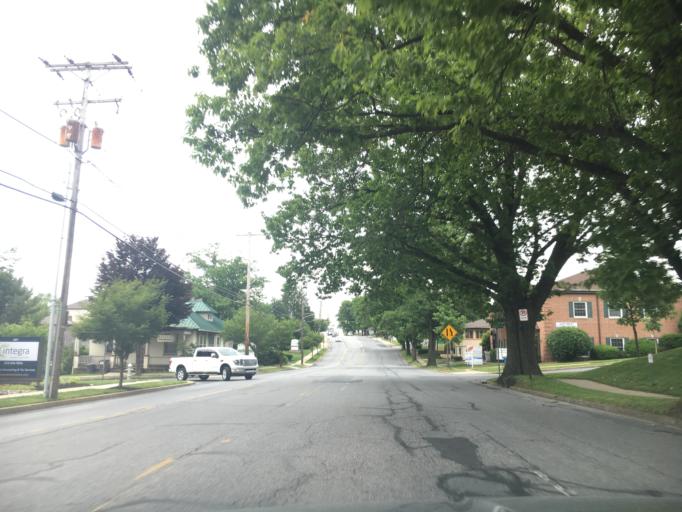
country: US
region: Pennsylvania
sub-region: Berks County
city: West Reading
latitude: 40.3433
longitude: -75.9577
